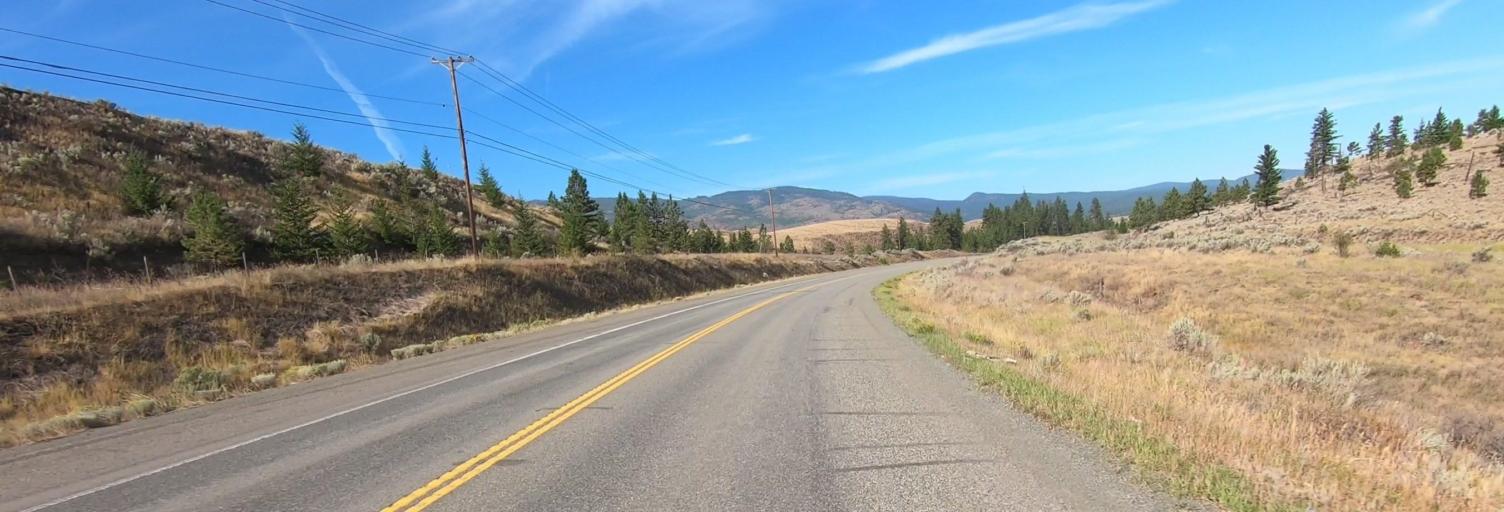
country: CA
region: British Columbia
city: Kamloops
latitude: 50.6611
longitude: -120.5320
